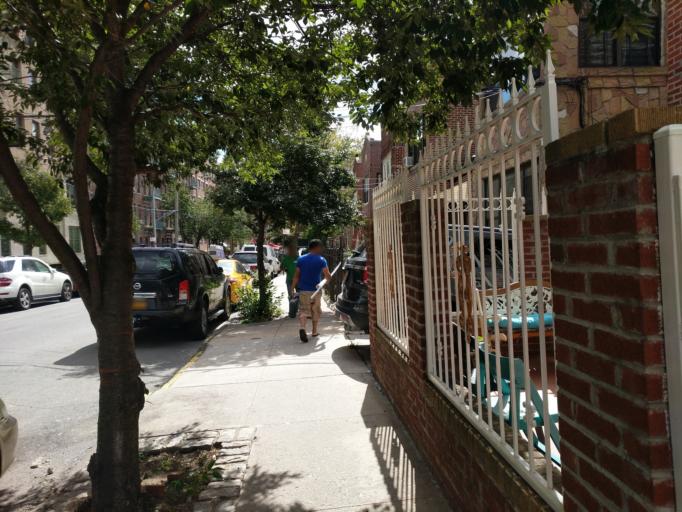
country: US
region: New York
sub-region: New York County
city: Inwood
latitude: 40.8431
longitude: -73.9216
